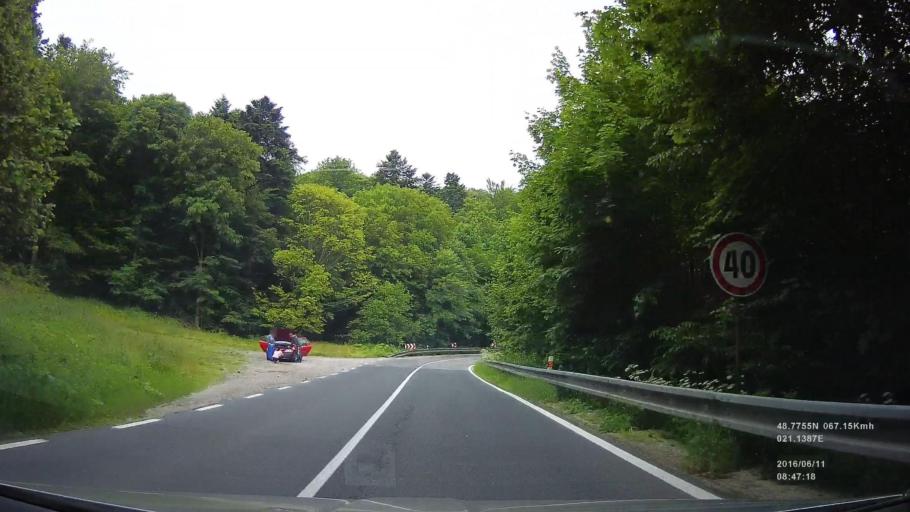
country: SK
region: Kosicky
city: Kosice
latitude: 48.7808
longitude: 21.1412
